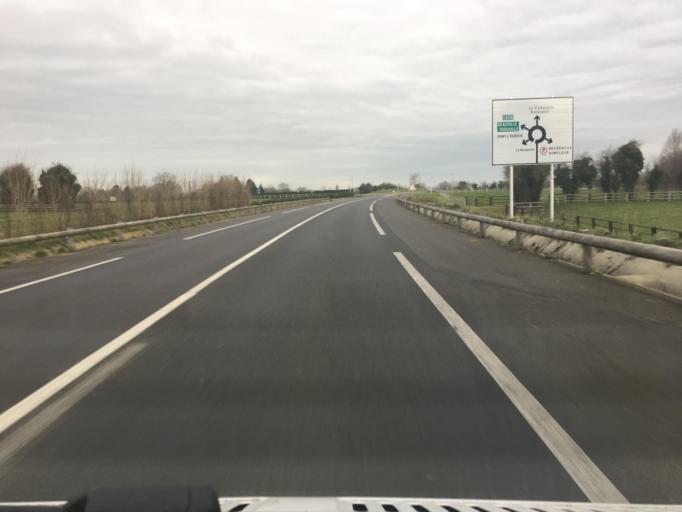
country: FR
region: Haute-Normandie
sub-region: Departement de l'Eure
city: Beuzeville
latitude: 49.3301
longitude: 0.3155
